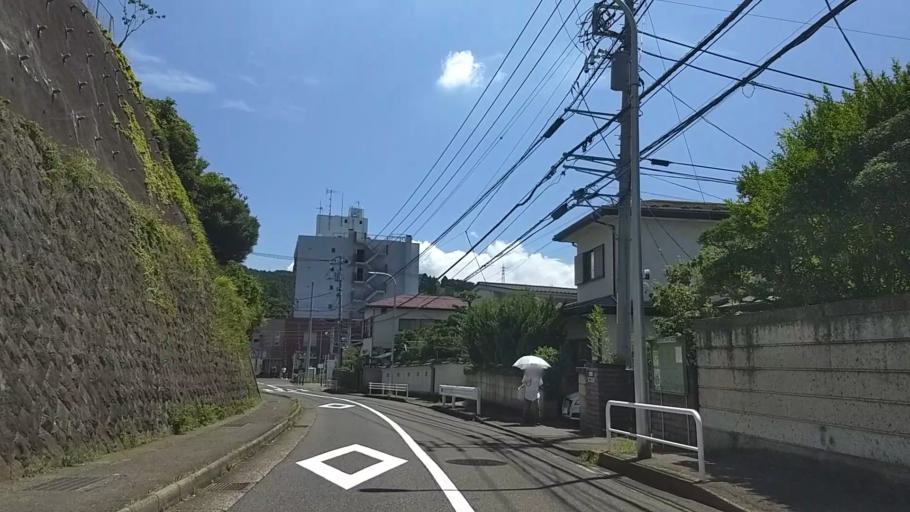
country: JP
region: Kanagawa
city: Zushi
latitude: 35.2998
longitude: 139.6006
